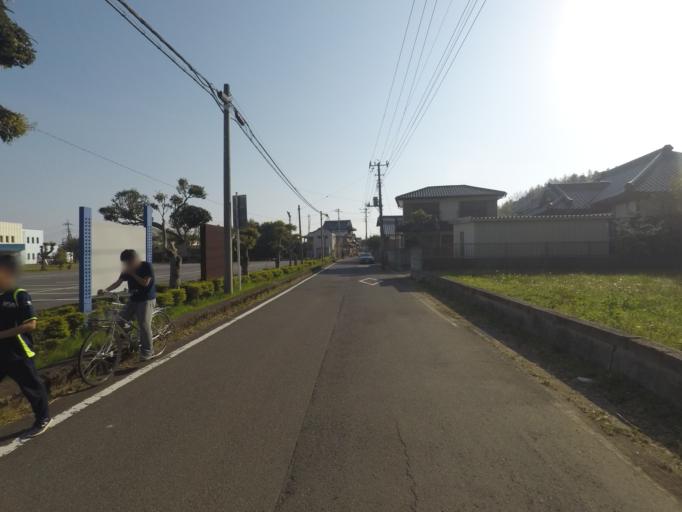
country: JP
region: Ibaraki
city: Inashiki
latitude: 36.0710
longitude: 140.3746
